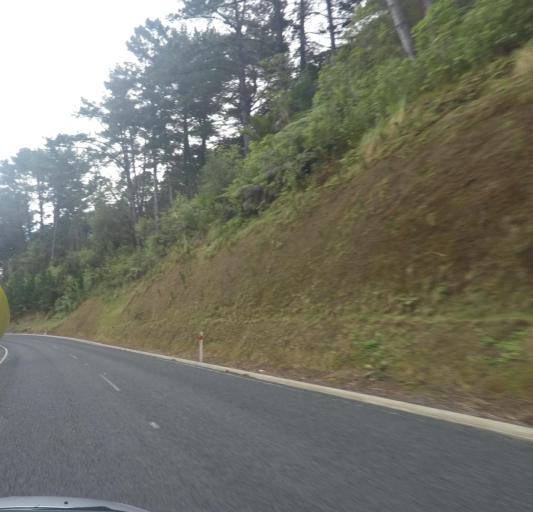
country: NZ
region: Auckland
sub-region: Auckland
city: Warkworth
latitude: -36.3742
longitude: 174.8020
